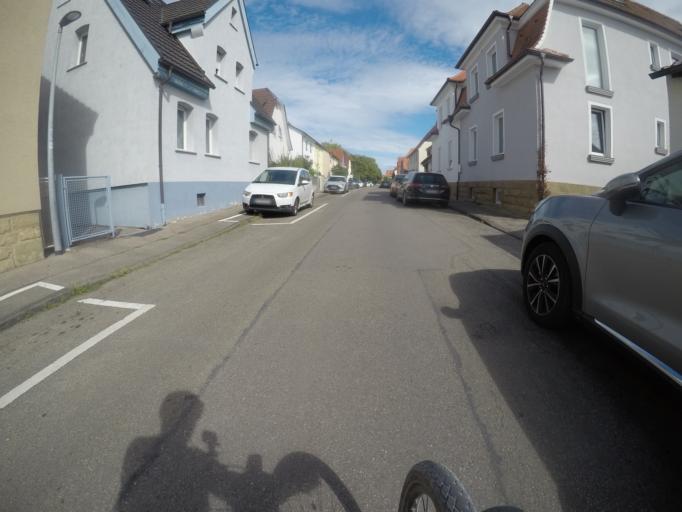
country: DE
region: Baden-Wuerttemberg
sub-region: Regierungsbezirk Stuttgart
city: Asperg
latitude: 48.9064
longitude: 9.1301
